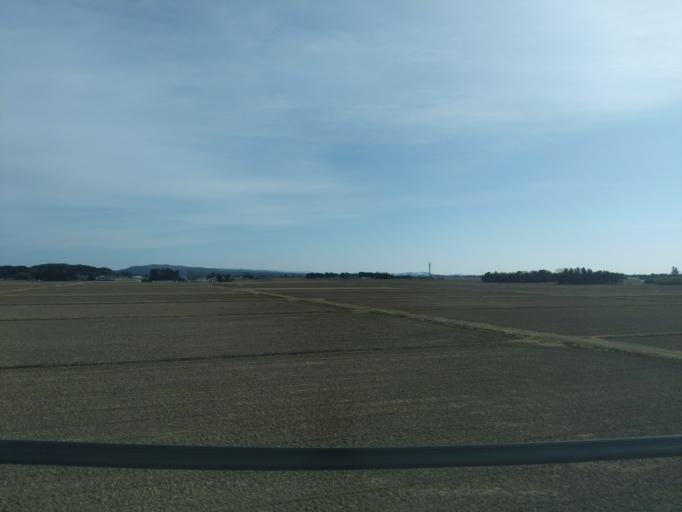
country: JP
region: Miyagi
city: Furukawa
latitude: 38.6112
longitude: 140.9904
